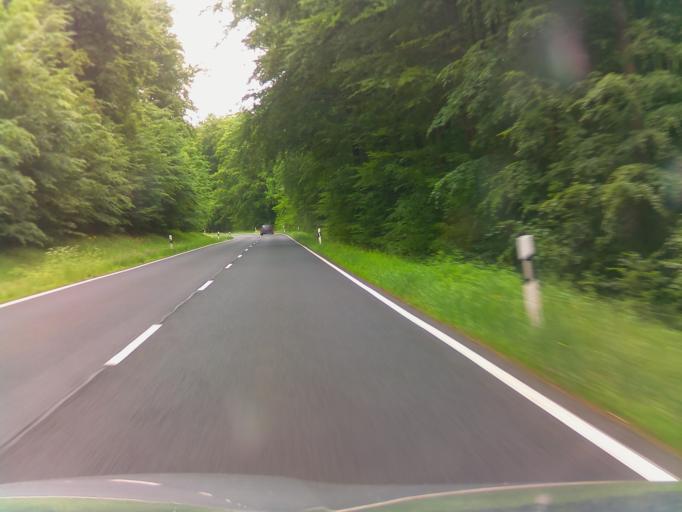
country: DE
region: Bavaria
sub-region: Regierungsbezirk Unterfranken
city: Schondra
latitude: 50.2363
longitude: 9.8243
